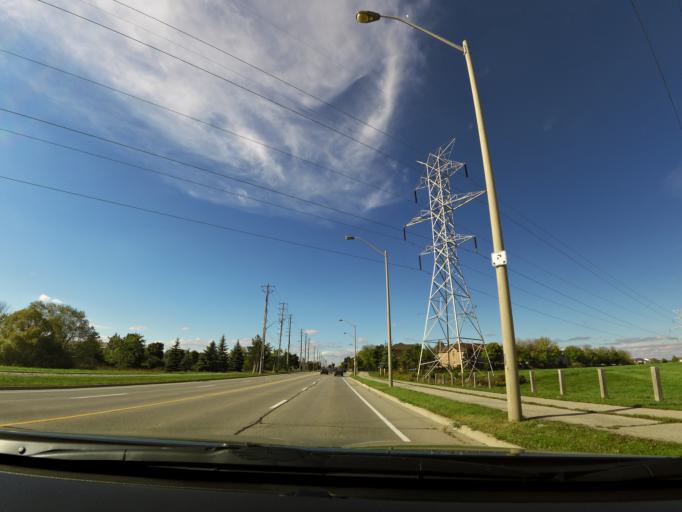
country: CA
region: Ontario
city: Burlington
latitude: 43.3873
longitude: -79.8173
